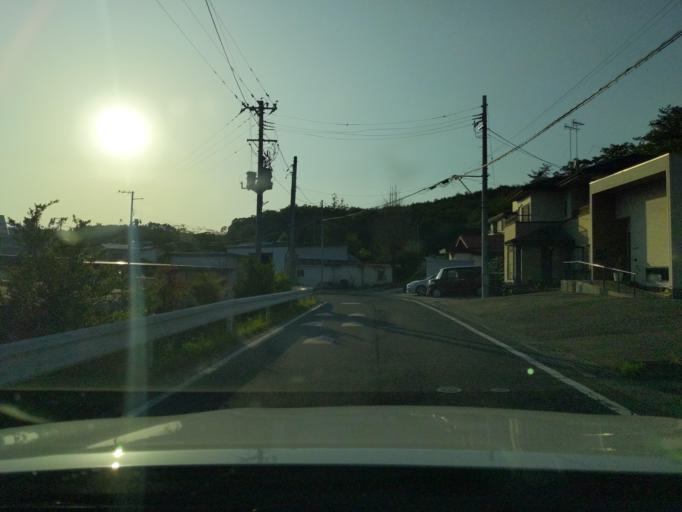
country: JP
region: Fukushima
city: Motomiya
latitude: 37.4846
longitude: 140.3678
